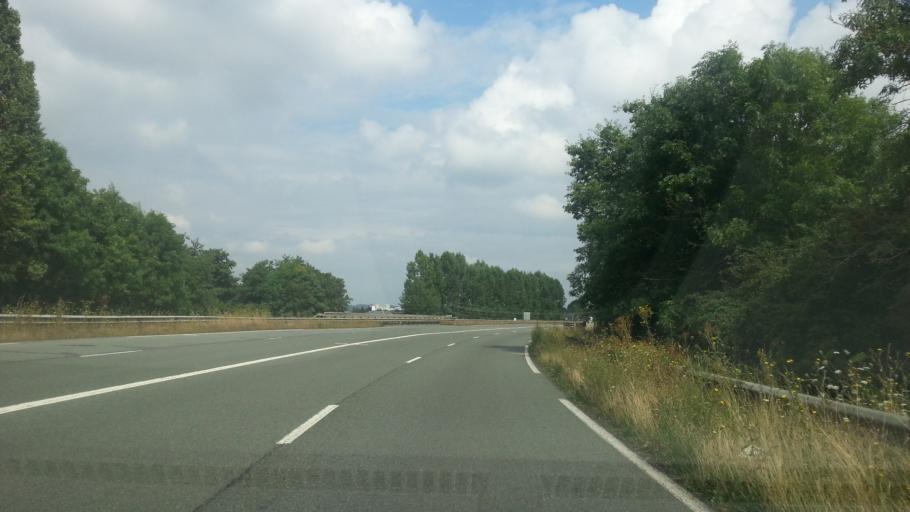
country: FR
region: Picardie
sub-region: Departement de l'Oise
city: Thiverny
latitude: 49.2524
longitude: 2.4421
